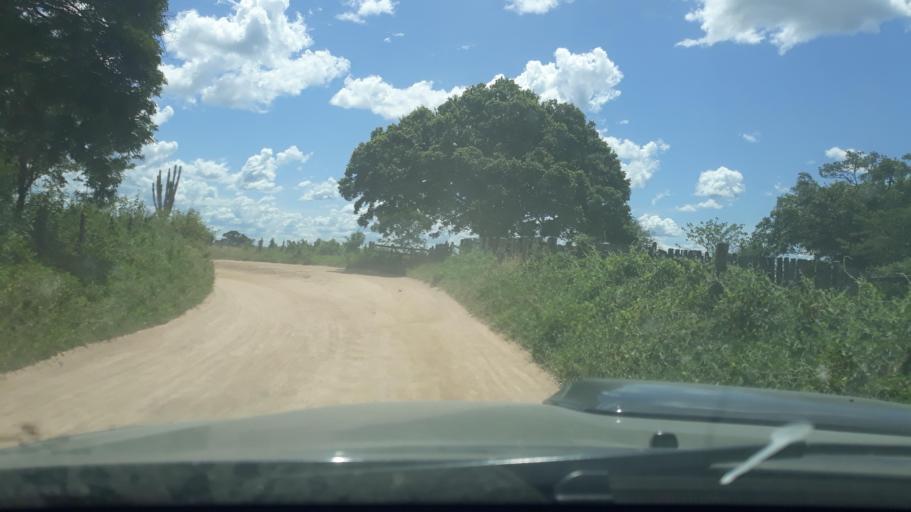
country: BR
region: Bahia
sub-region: Riacho De Santana
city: Riacho de Santana
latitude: -13.9100
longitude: -42.9512
